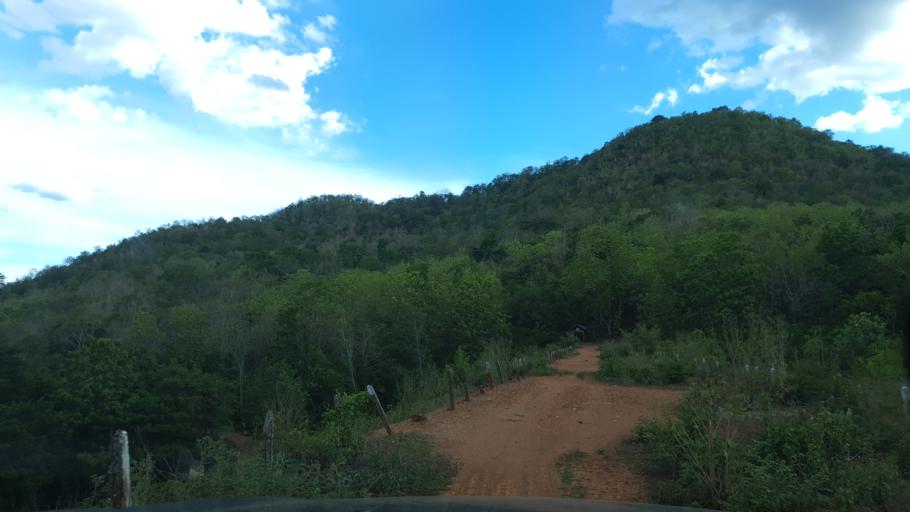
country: TH
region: Lampang
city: Sop Prap
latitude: 17.8890
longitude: 99.2843
